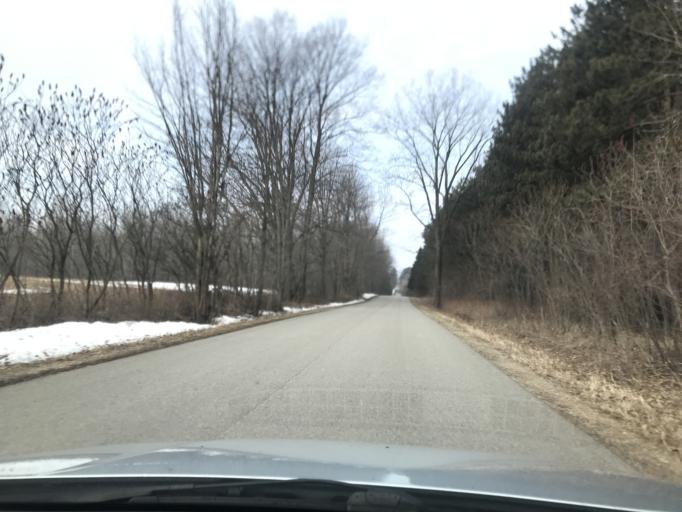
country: US
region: Wisconsin
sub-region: Oconto County
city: Oconto Falls
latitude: 44.8294
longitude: -88.1732
